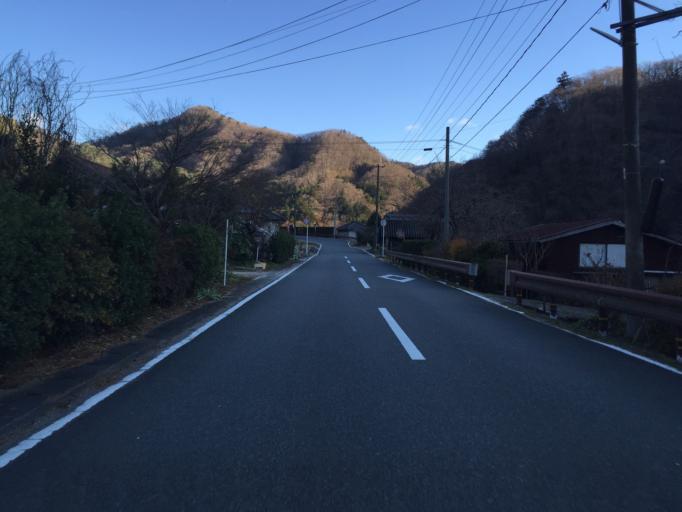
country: JP
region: Fukushima
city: Iwaki
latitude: 37.1791
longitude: 140.8257
